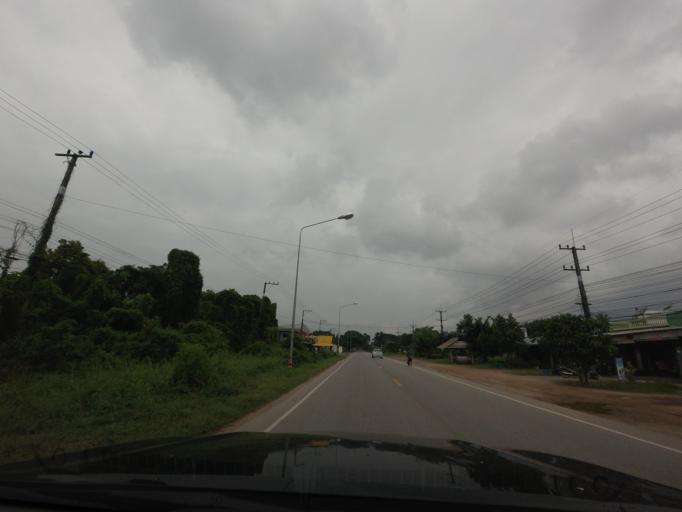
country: TH
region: Nong Khai
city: Si Chiang Mai
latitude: 17.9578
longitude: 102.5631
